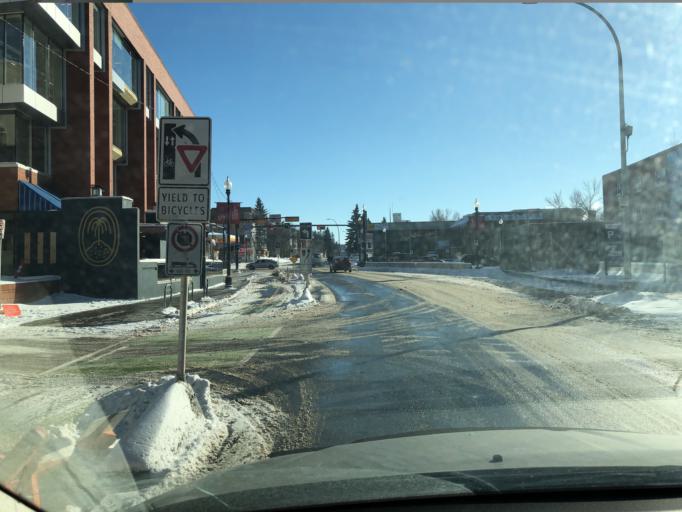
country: CA
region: Alberta
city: Calgary
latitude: 51.0385
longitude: -114.0744
